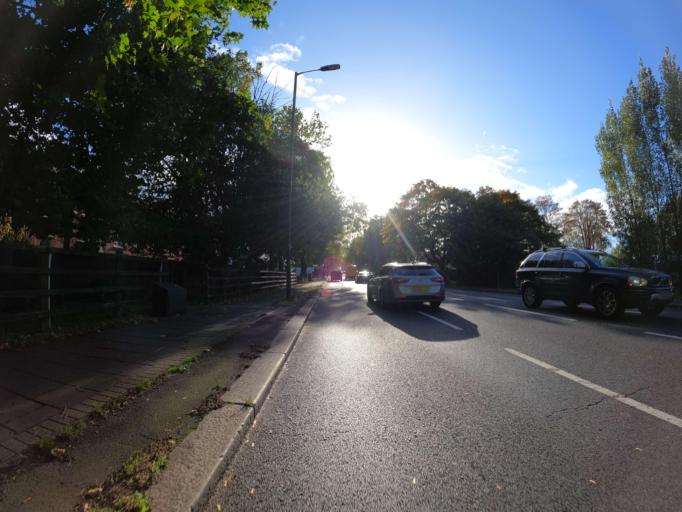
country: GB
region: England
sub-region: Greater London
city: Acton
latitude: 51.4805
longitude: -0.2595
